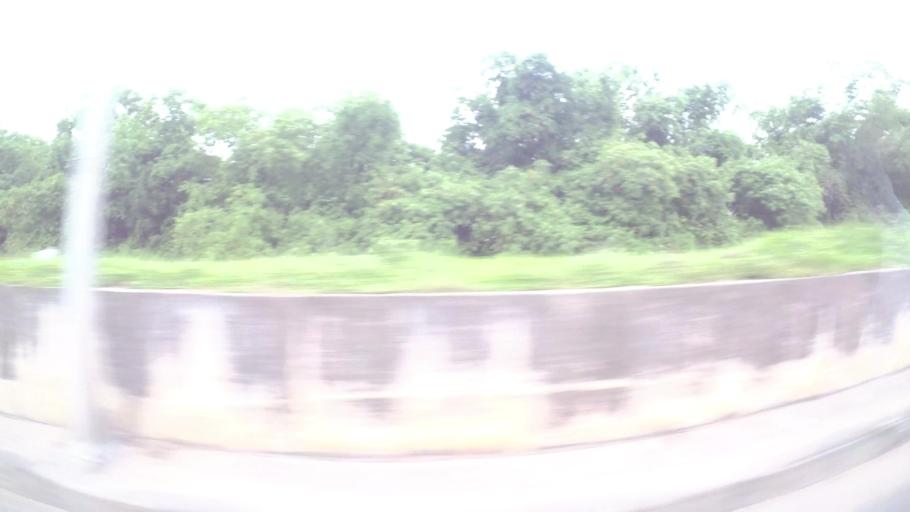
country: VN
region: Ha Noi
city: Trau Quy
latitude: 21.0493
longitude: 105.9258
